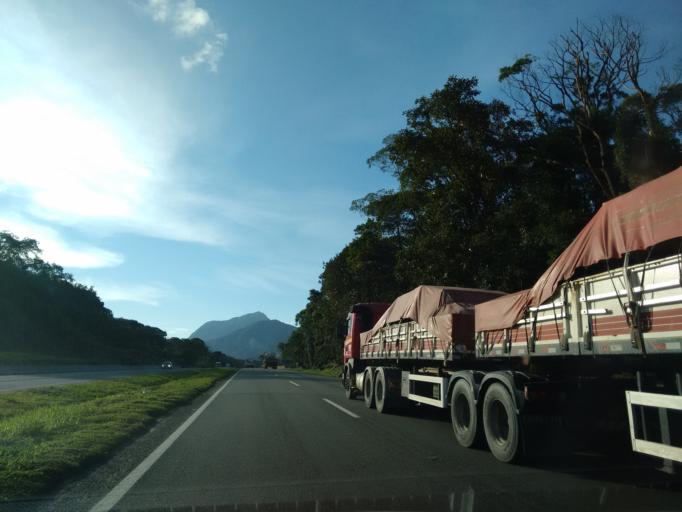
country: BR
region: Santa Catarina
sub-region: Joinville
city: Joinville
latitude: -26.0251
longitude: -48.8615
